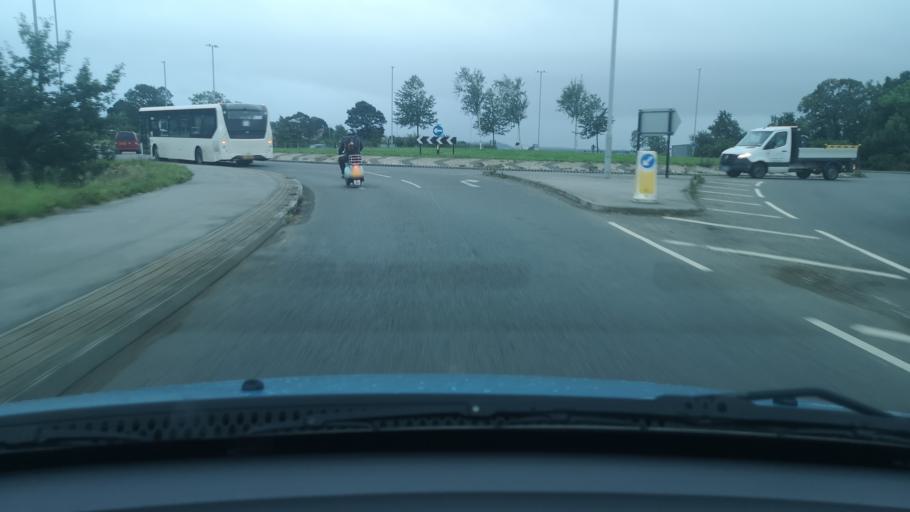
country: GB
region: England
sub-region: City and Borough of Wakefield
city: North Elmsall
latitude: 53.6087
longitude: -1.2874
